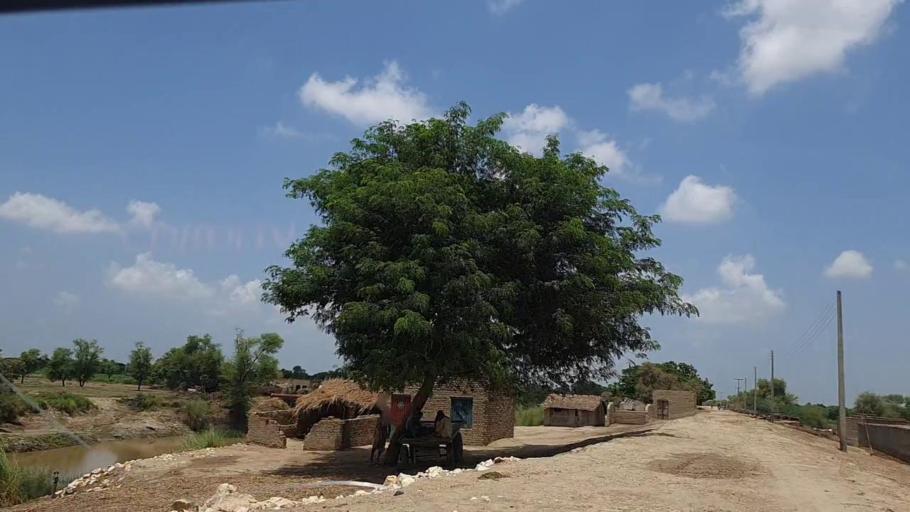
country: PK
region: Sindh
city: Tharu Shah
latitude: 26.9217
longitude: 67.9896
